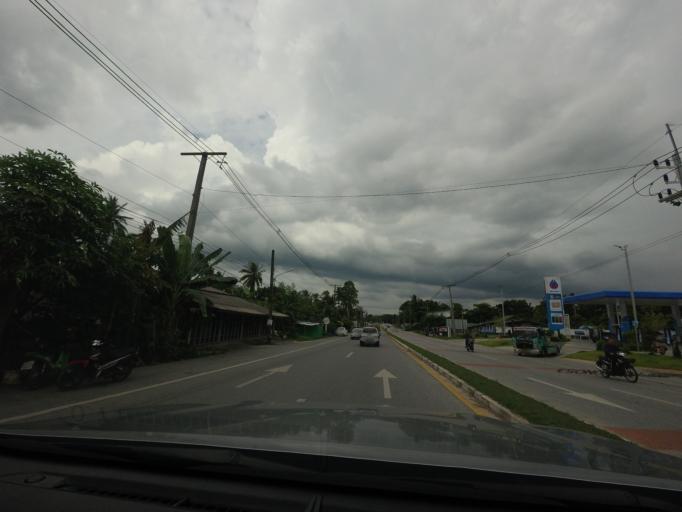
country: TH
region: Yala
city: Raman
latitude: 6.4755
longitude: 101.4338
